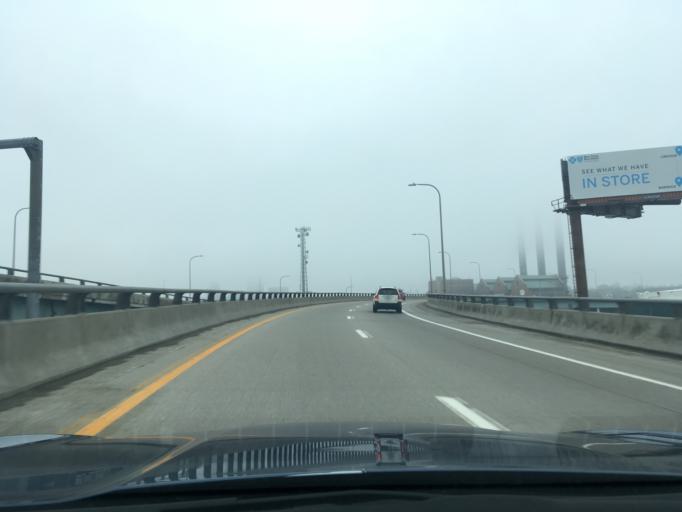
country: US
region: Rhode Island
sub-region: Providence County
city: Providence
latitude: 41.8114
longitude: -71.4049
